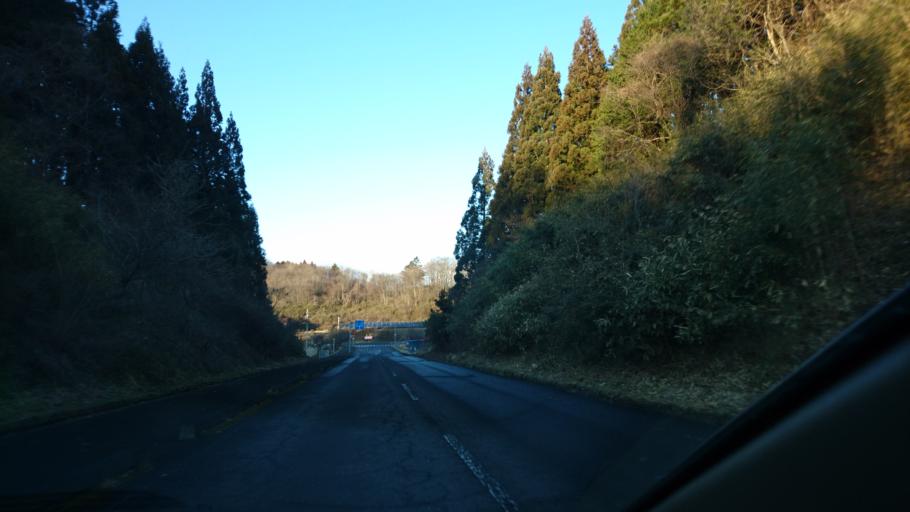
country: JP
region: Miyagi
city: Furukawa
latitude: 38.6911
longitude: 140.9266
